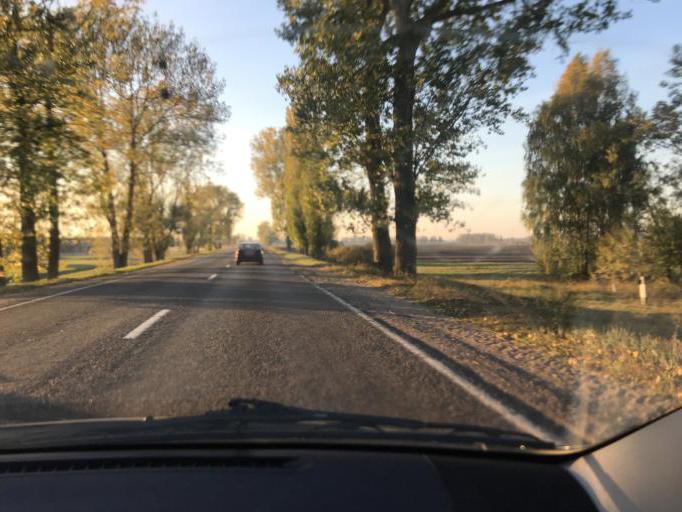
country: BY
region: Brest
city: Pinsk
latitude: 52.0664
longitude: 26.1900
